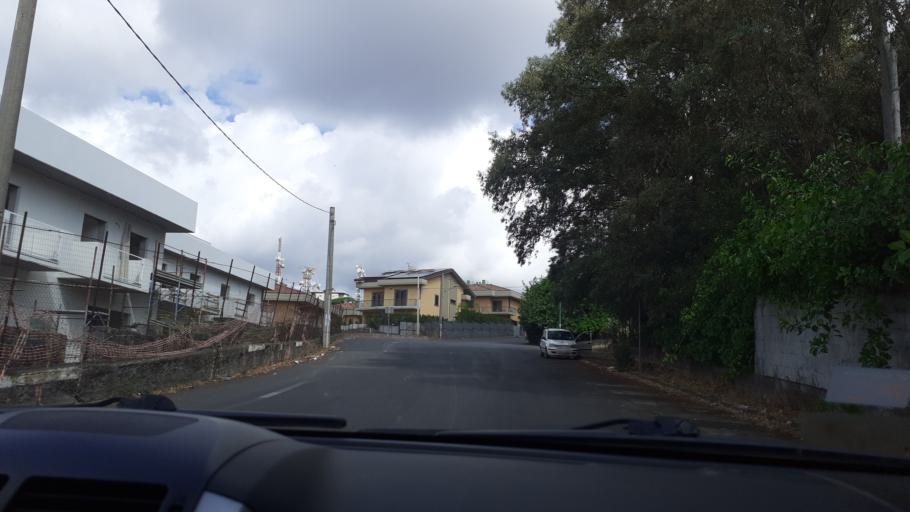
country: IT
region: Sicily
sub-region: Catania
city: Carrubazza-Motta
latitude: 37.5603
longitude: 15.1054
